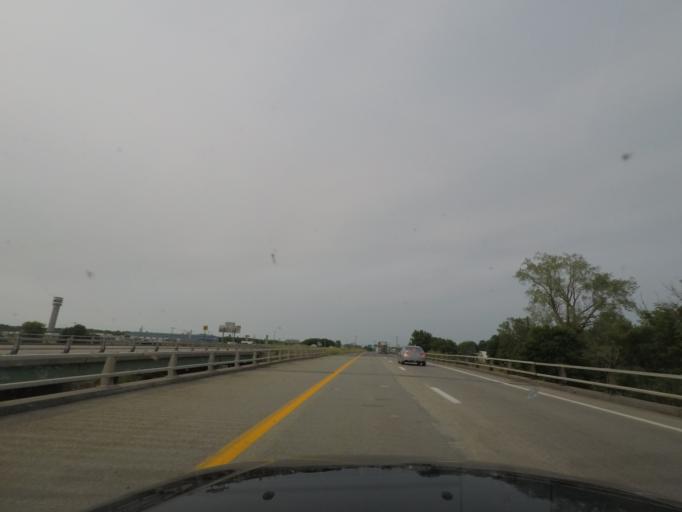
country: US
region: New York
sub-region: Clinton County
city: Champlain
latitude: 44.9917
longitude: -73.4565
